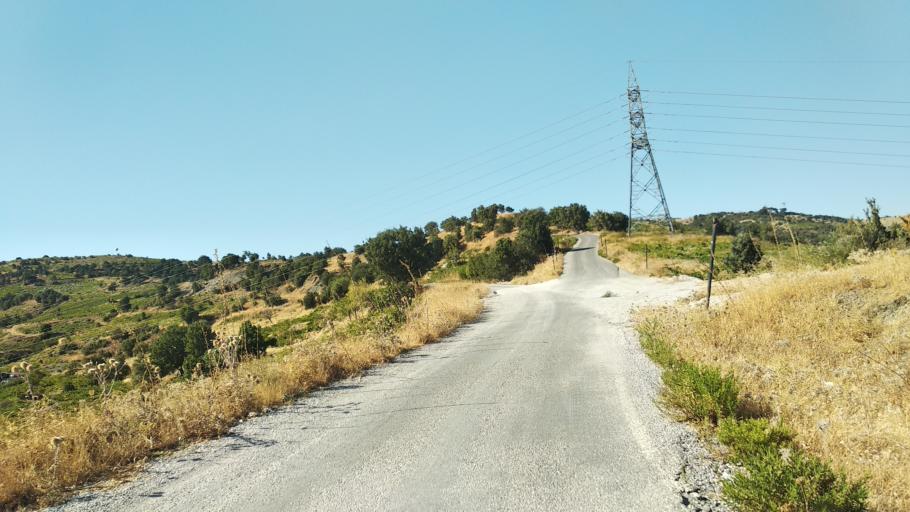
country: TR
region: Izmir
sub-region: Seferihisar
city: Seferhisar
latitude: 38.3263
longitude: 26.9510
